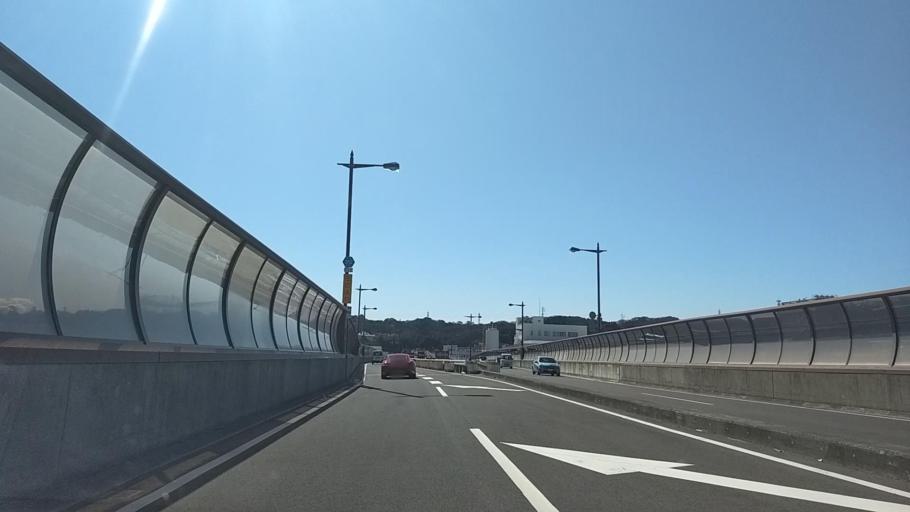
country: JP
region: Kanagawa
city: Fujisawa
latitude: 35.3366
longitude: 139.5018
